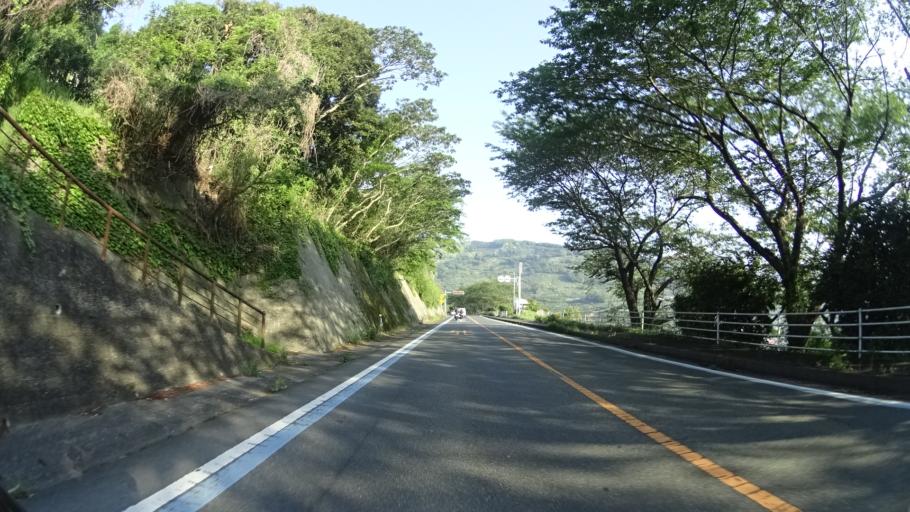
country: JP
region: Ehime
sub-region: Nishiuwa-gun
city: Ikata-cho
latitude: 33.4895
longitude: 132.3961
